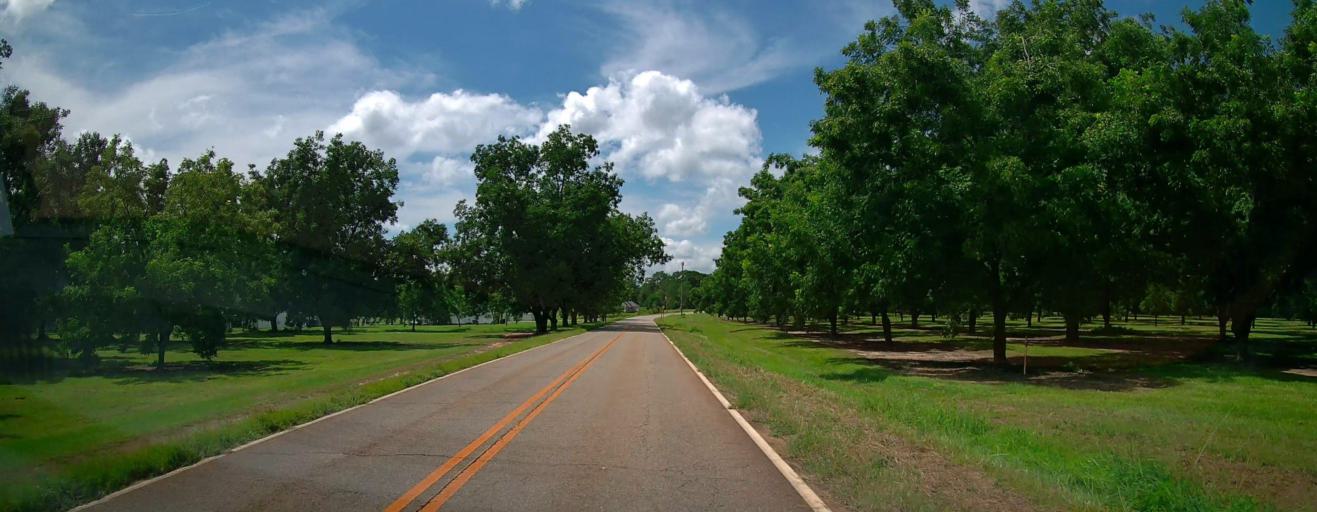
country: US
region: Georgia
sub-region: Houston County
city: Perry
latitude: 32.5212
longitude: -83.7942
